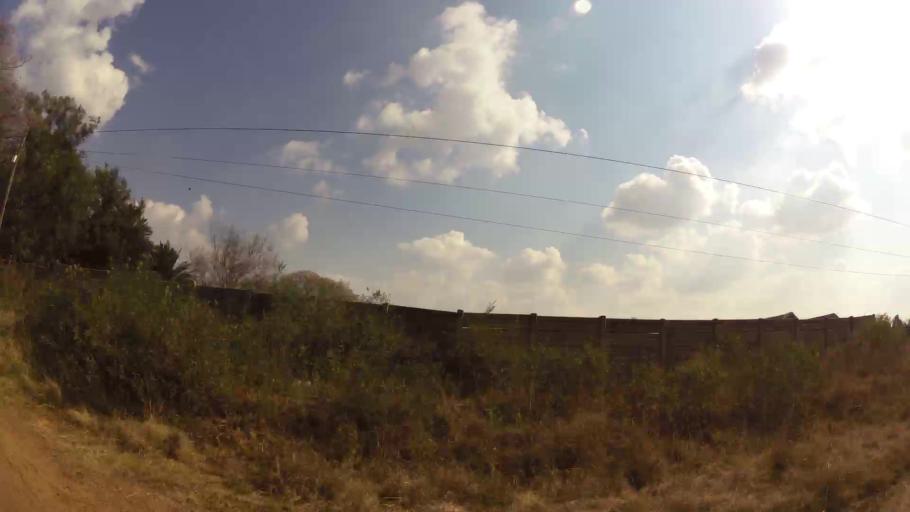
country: ZA
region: Mpumalanga
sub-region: Nkangala District Municipality
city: Delmas
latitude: -26.1719
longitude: 28.5454
